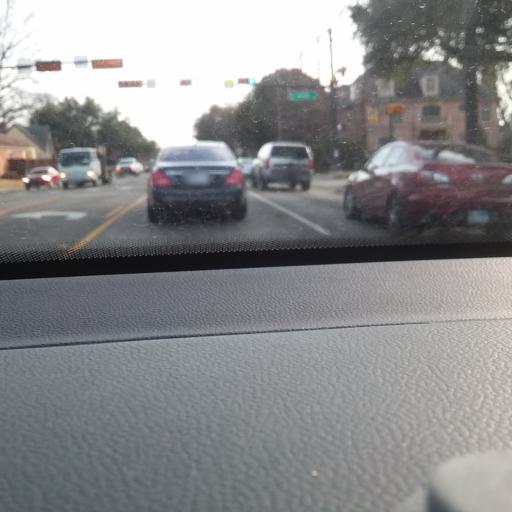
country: US
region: Texas
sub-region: Dallas County
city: University Park
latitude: 32.8534
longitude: -96.8045
